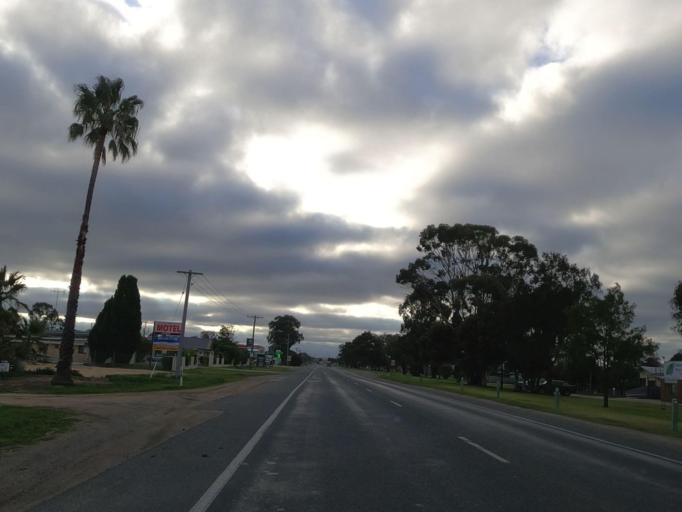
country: AU
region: Victoria
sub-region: Swan Hill
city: Swan Hill
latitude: -35.7413
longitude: 143.9201
